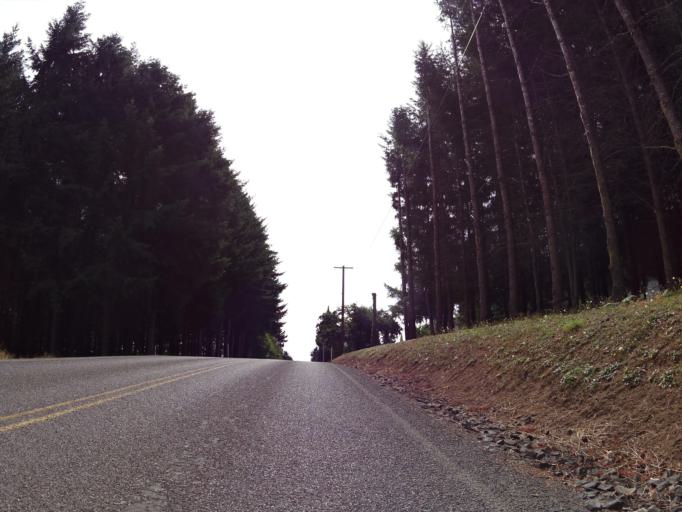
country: US
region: Washington
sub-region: Lewis County
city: Winlock
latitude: 46.5198
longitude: -122.9496
